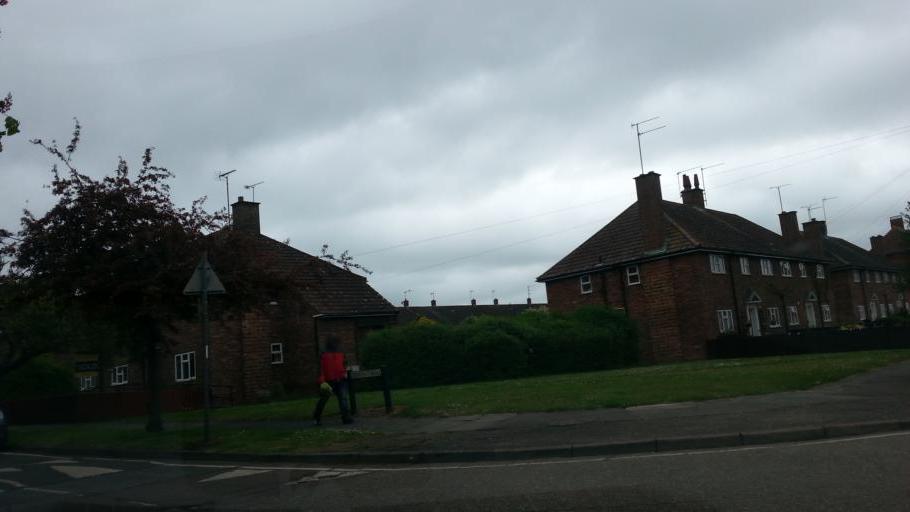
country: GB
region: England
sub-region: Suffolk
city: Bury St Edmunds
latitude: 52.2640
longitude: 0.7027
